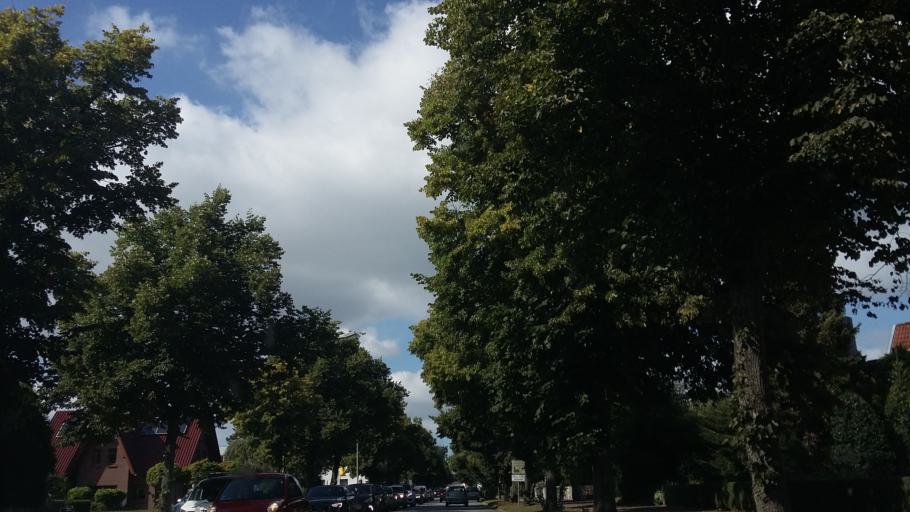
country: DE
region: Lower Saxony
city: Loxstedt
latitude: 53.4971
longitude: 8.6012
